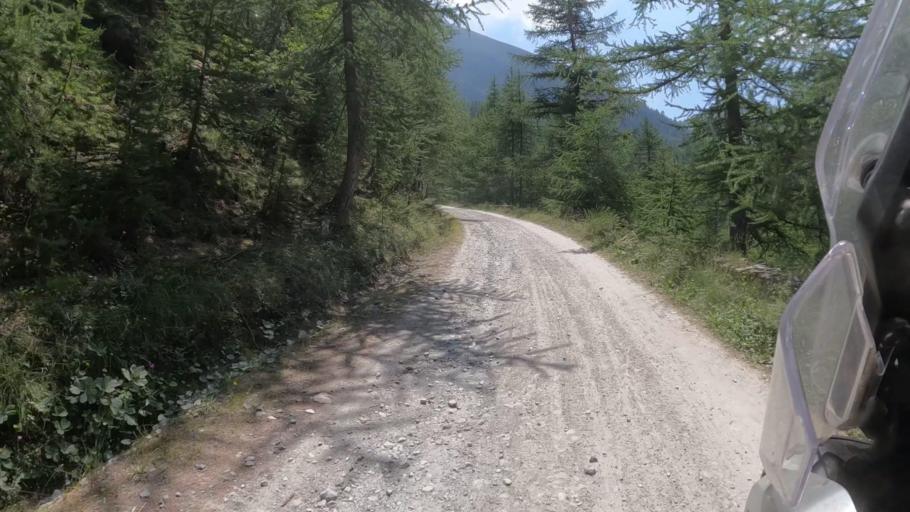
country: IT
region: Piedmont
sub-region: Provincia di Torino
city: Meana di Susa
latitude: 45.0826
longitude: 7.0589
